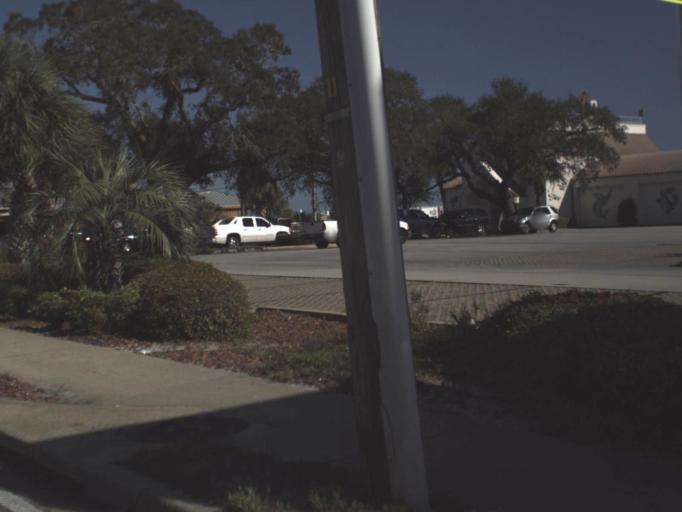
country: US
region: Florida
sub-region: Okaloosa County
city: Destin
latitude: 30.3932
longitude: -86.5013
